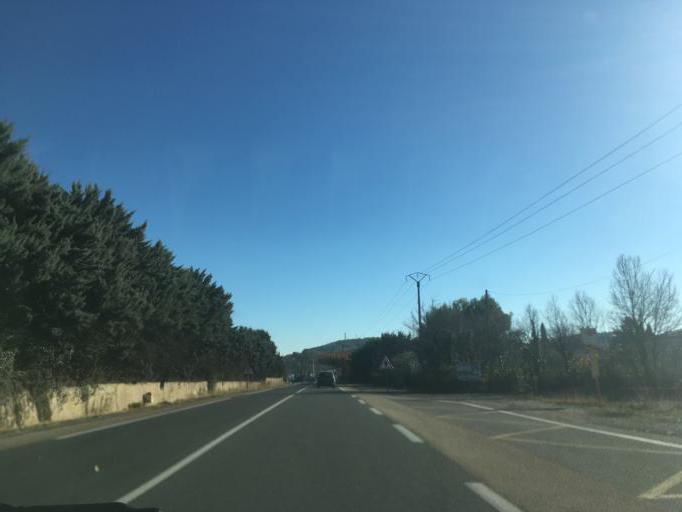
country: FR
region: Provence-Alpes-Cote d'Azur
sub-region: Departement du Var
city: Flayosc
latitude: 43.5286
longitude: 6.4284
